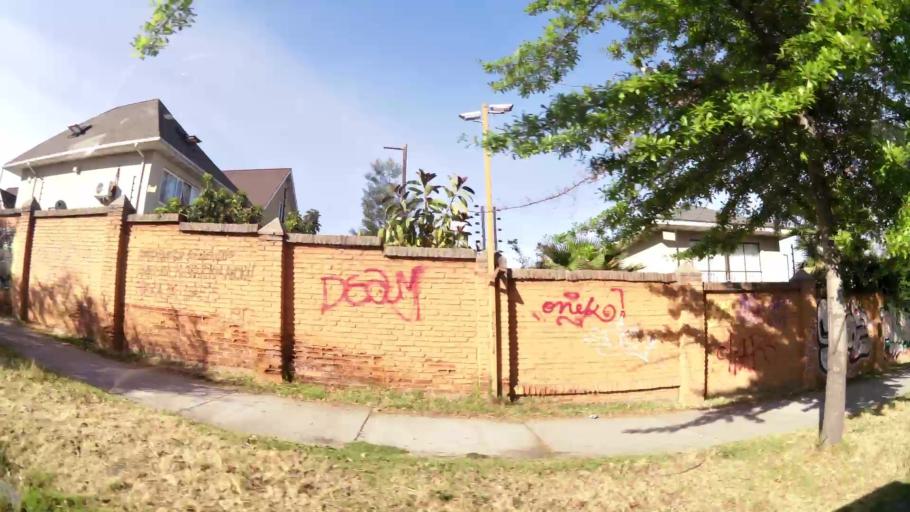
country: CL
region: Santiago Metropolitan
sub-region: Provincia de Santiago
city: Villa Presidente Frei, Nunoa, Santiago, Chile
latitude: -33.4884
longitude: -70.5517
